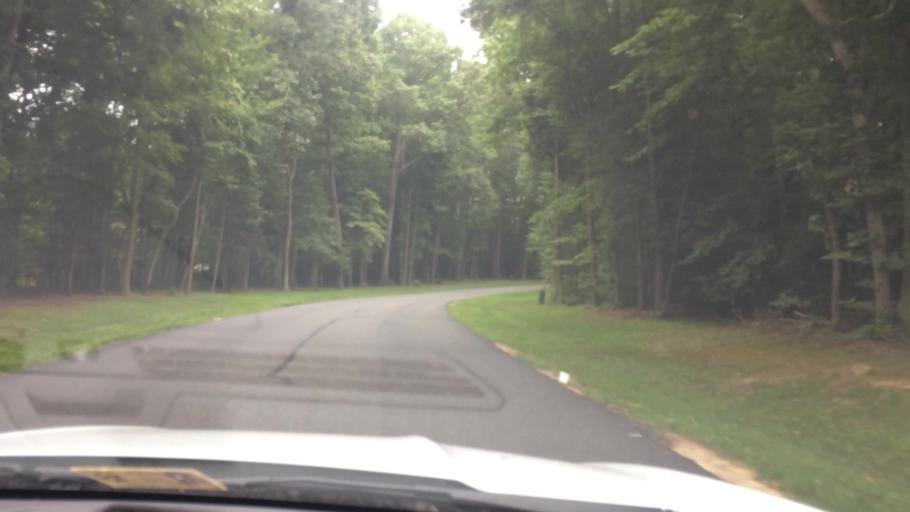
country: US
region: Virginia
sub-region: James City County
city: Williamsburg
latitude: 37.2963
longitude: -76.7812
